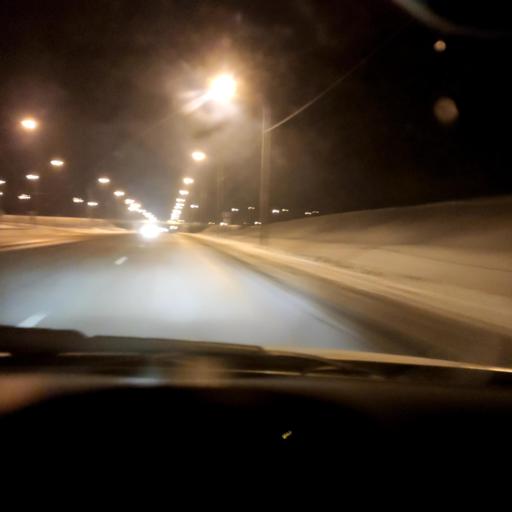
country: RU
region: Kursk
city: Fatezh
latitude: 52.0954
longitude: 35.8206
